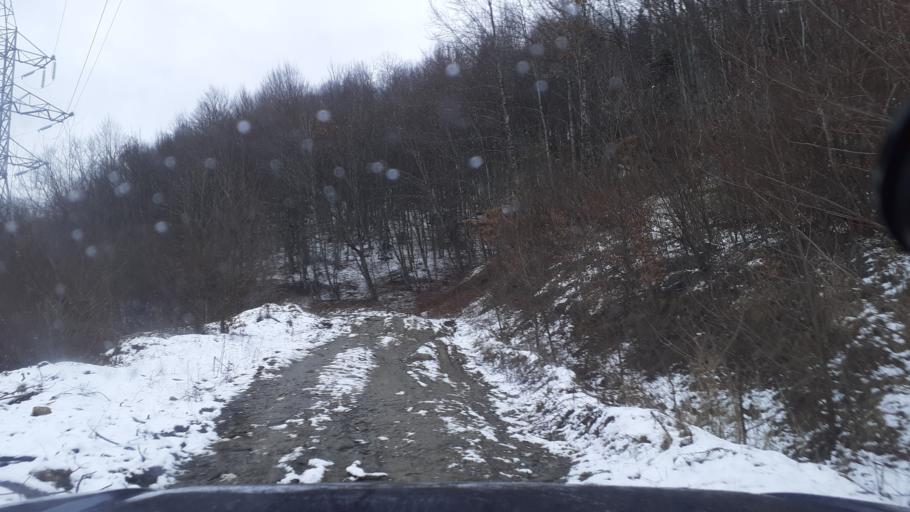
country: RU
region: Adygeya
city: Kamennomostskiy
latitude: 44.1095
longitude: 40.1083
